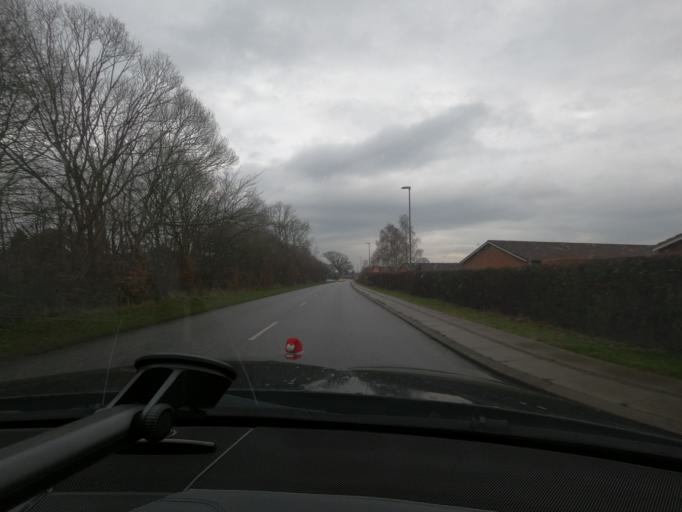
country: DK
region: South Denmark
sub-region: Sonderborg Kommune
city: Horuphav
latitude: 54.9159
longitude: 9.8954
